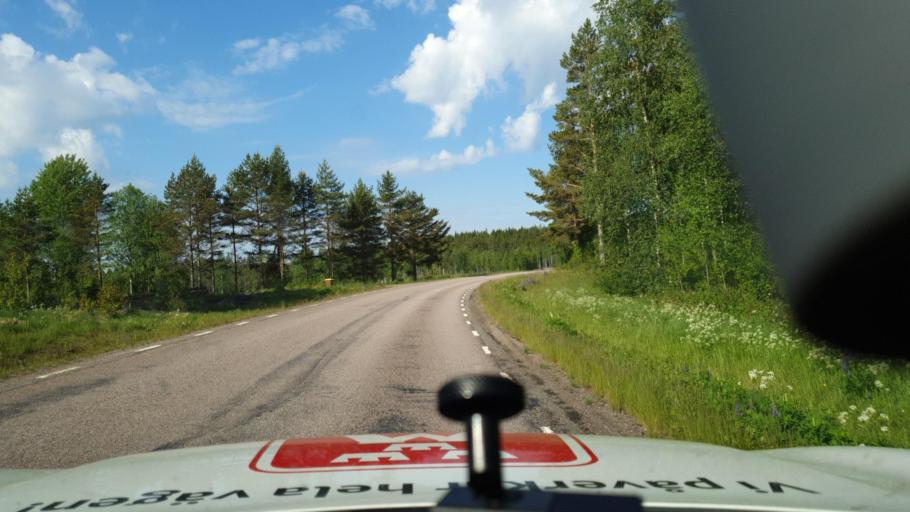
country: SE
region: Vaermland
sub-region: Arvika Kommun
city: Arvika
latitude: 59.9526
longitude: 12.7076
